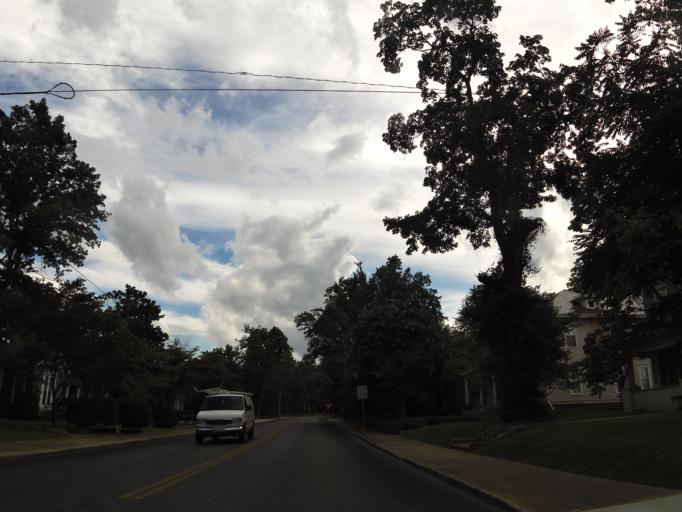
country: US
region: Kentucky
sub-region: Christian County
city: Hopkinsville
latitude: 36.8586
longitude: -87.4936
